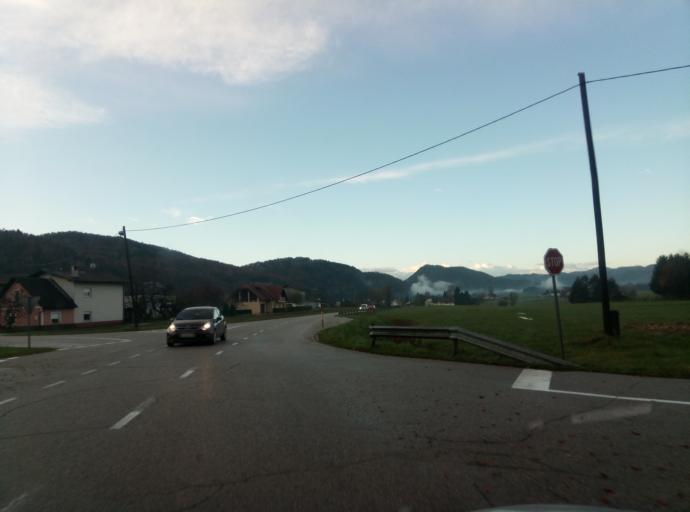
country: SI
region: Vodice
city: Vodice
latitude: 46.1639
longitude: 14.5168
